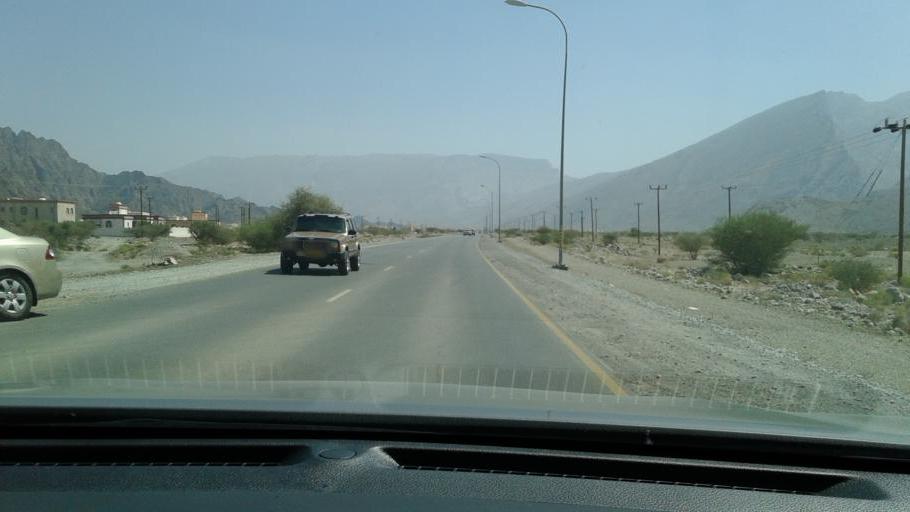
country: OM
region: Al Batinah
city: Rustaq
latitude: 23.3581
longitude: 57.4814
